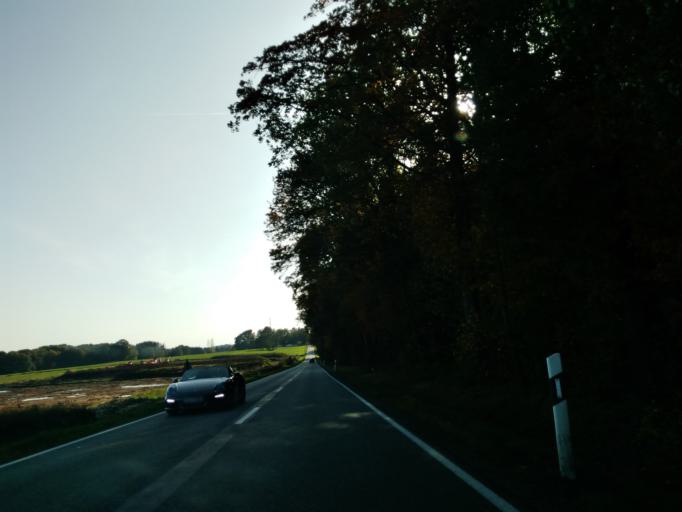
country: DE
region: Rheinland-Pfalz
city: Windhagen
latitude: 50.6680
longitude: 7.3623
